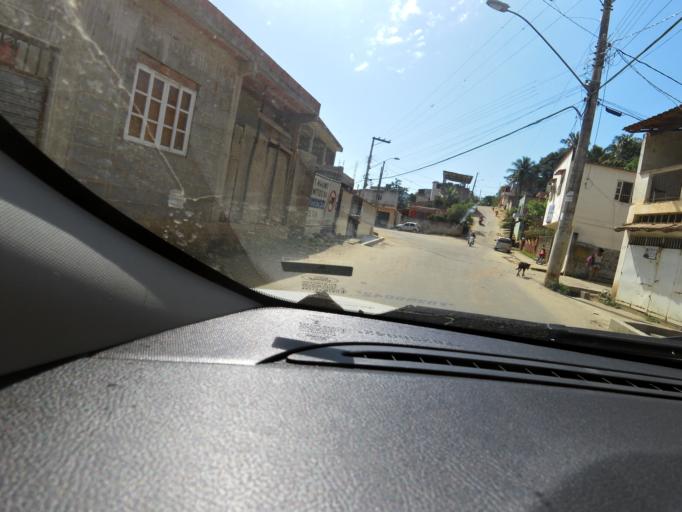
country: BR
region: Espirito Santo
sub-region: Guarapari
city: Guarapari
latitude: -20.6593
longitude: -40.5209
